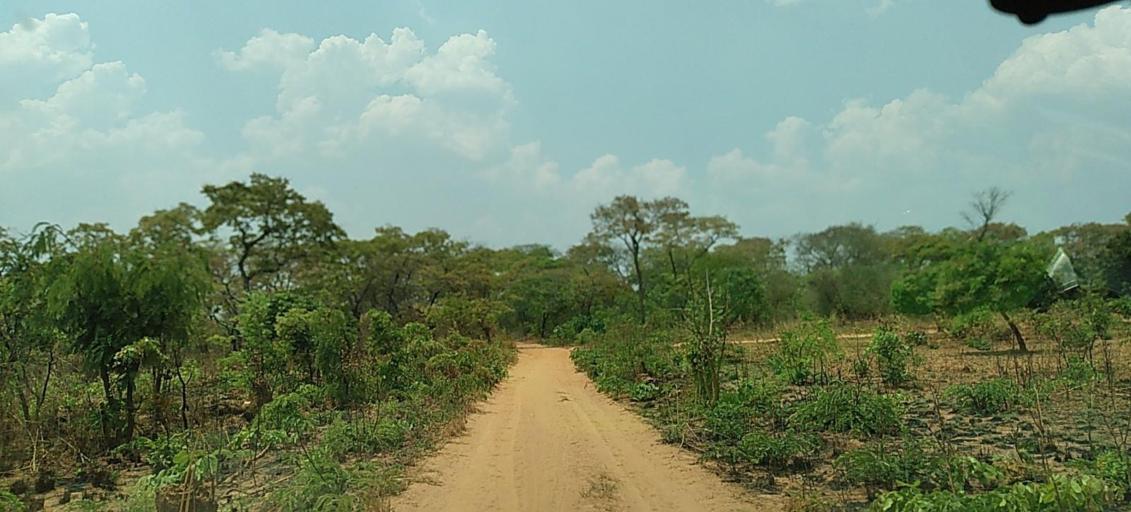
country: ZM
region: North-Western
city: Kabompo
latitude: -13.6467
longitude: 24.3770
